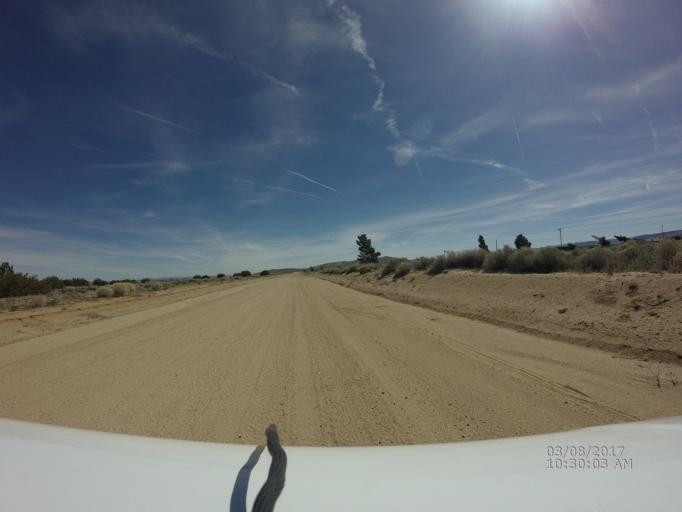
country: US
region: California
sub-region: Los Angeles County
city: Green Valley
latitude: 34.7603
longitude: -118.4519
